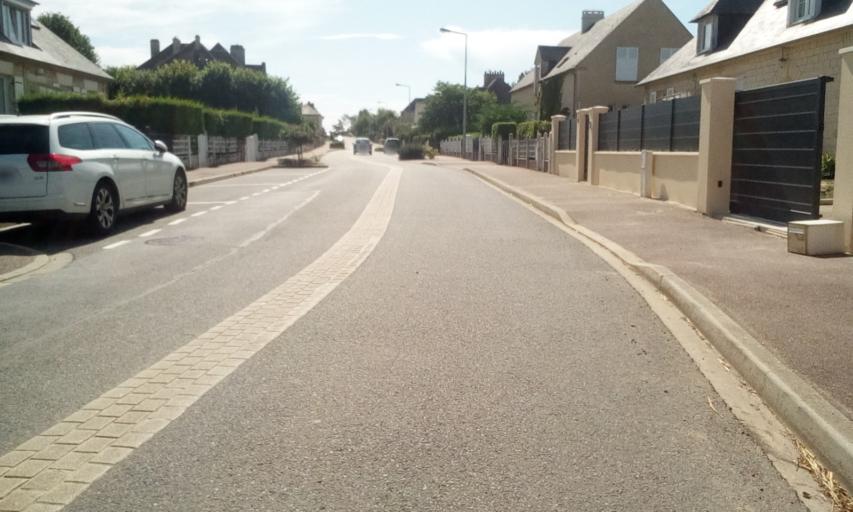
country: FR
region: Lower Normandy
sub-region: Departement du Calvados
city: Eterville
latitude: 49.1301
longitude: -0.4210
